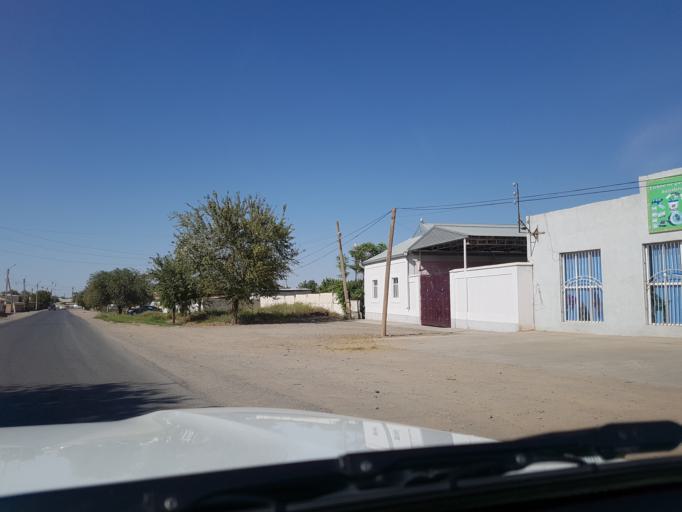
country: IR
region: Razavi Khorasan
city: Sarakhs
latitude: 36.5208
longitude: 61.2184
